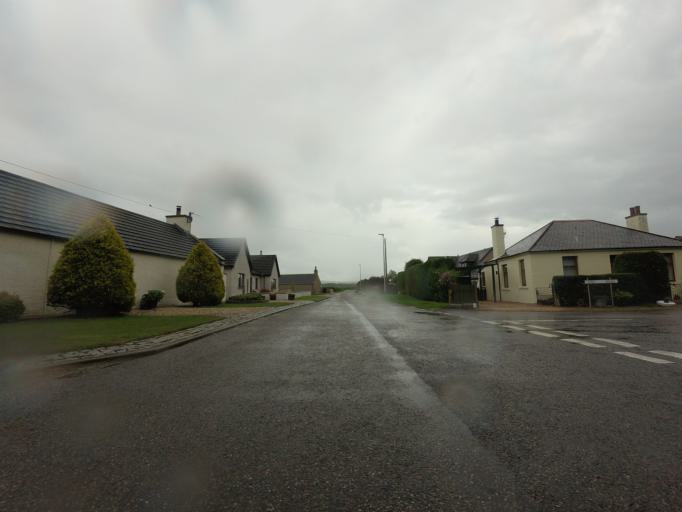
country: GB
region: Scotland
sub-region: Moray
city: Fochabers
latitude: 57.6604
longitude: -3.0734
